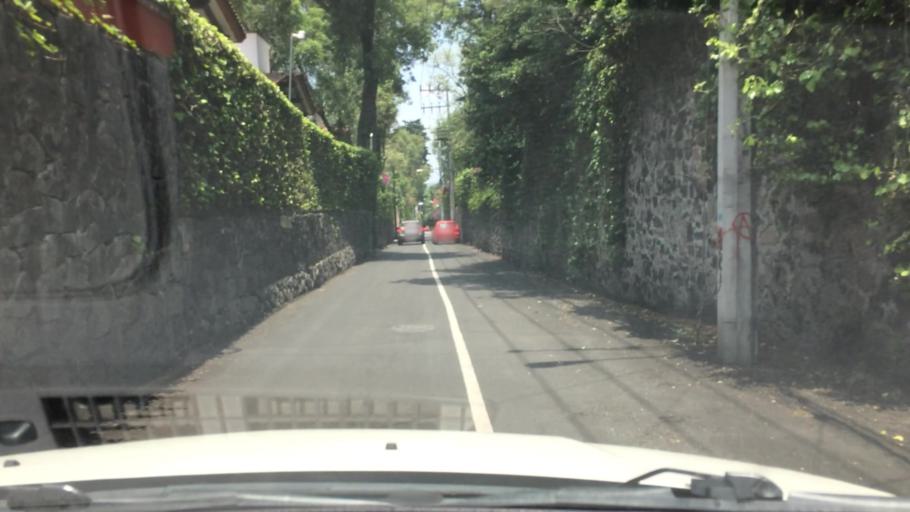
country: MX
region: Mexico City
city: Magdalena Contreras
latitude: 19.3271
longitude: -99.2224
